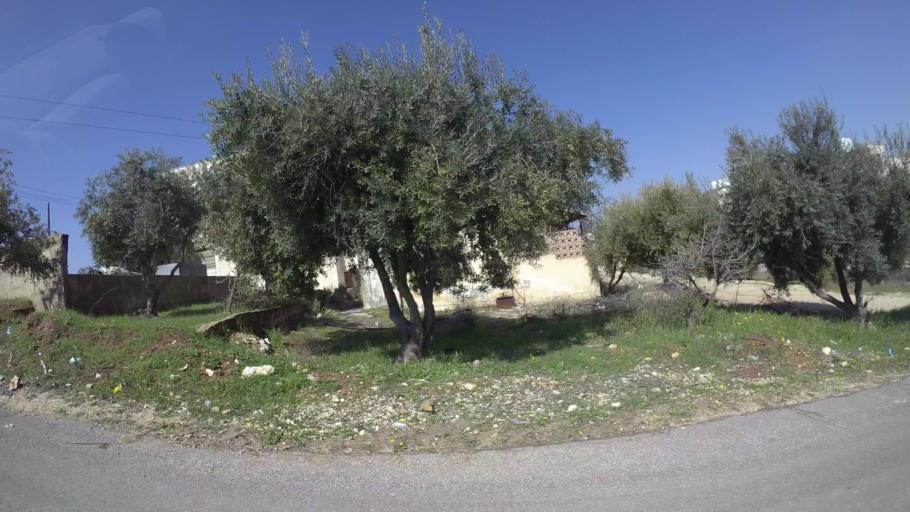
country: JO
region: Amman
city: Al Bunayyat ash Shamaliyah
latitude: 31.8971
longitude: 35.8957
